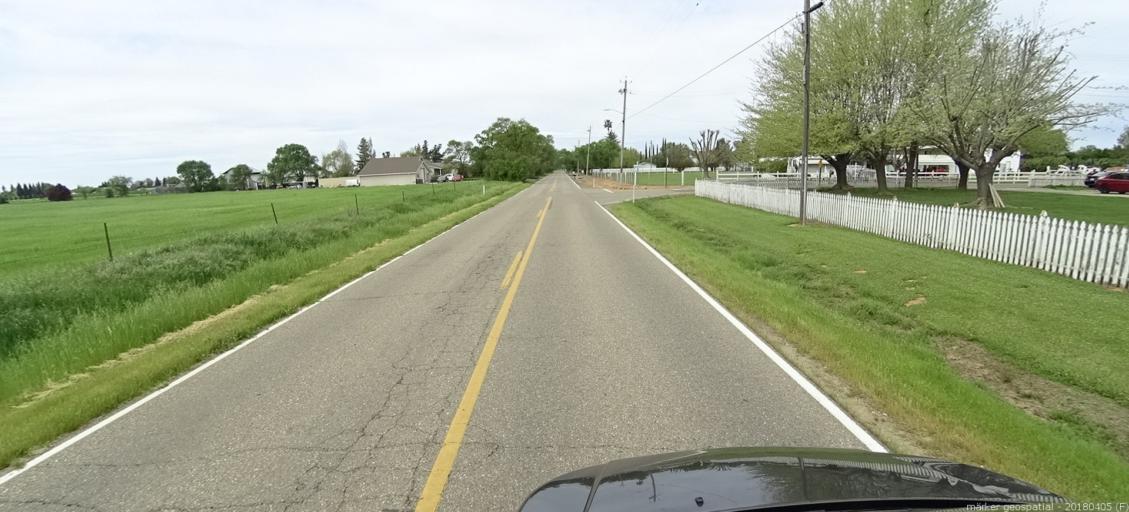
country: US
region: California
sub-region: Sacramento County
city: Galt
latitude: 38.2619
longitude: -121.3298
